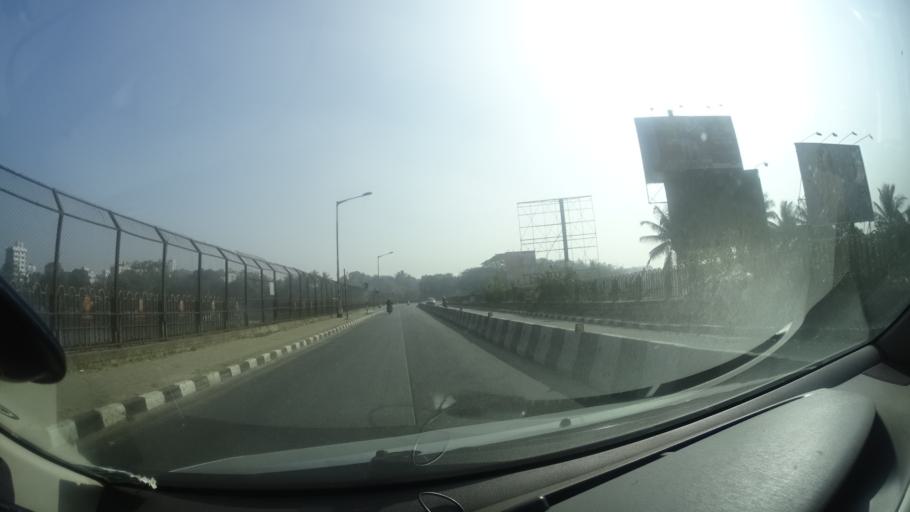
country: IN
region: Karnataka
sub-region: Bangalore Urban
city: Bangalore
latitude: 13.0076
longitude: 77.5745
